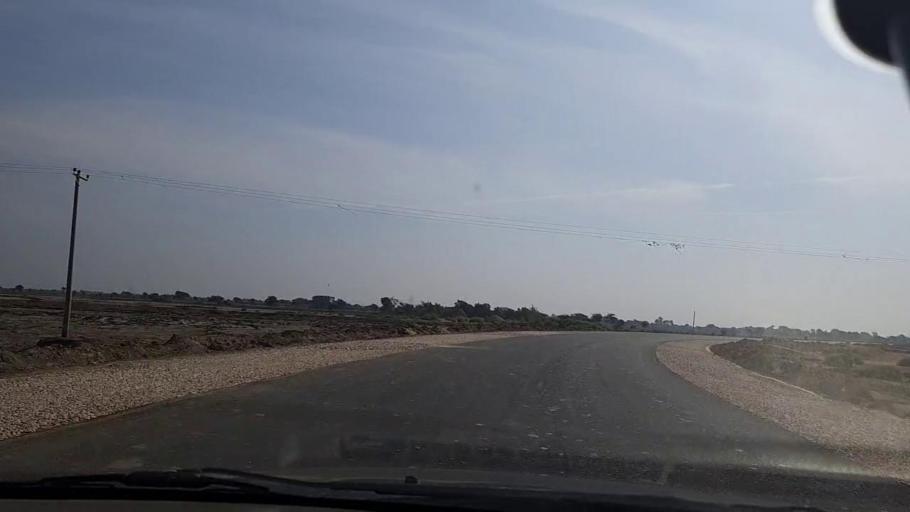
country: PK
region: Sindh
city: Mirpur Batoro
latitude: 24.7446
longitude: 68.2738
